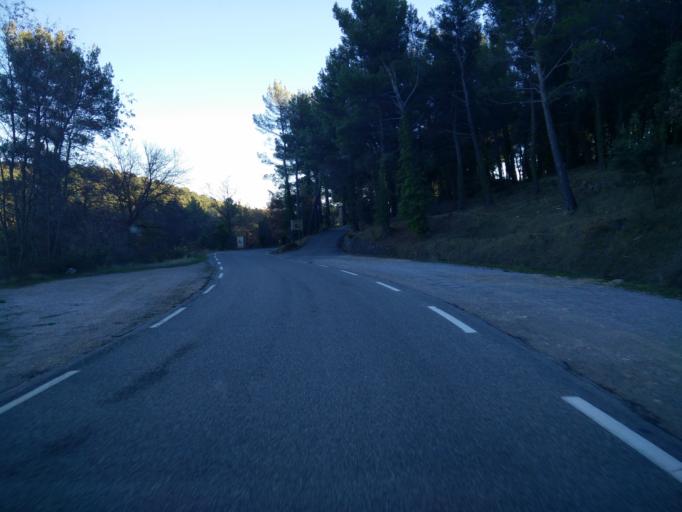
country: FR
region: Provence-Alpes-Cote d'Azur
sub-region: Departement du Var
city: Villecroze
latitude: 43.5880
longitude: 6.3070
